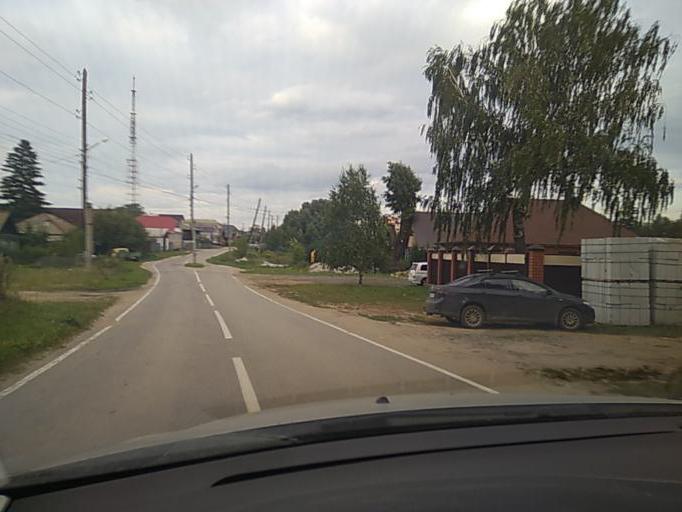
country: RU
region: Chelyabinsk
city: Kyshtym
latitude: 55.6940
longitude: 60.5456
